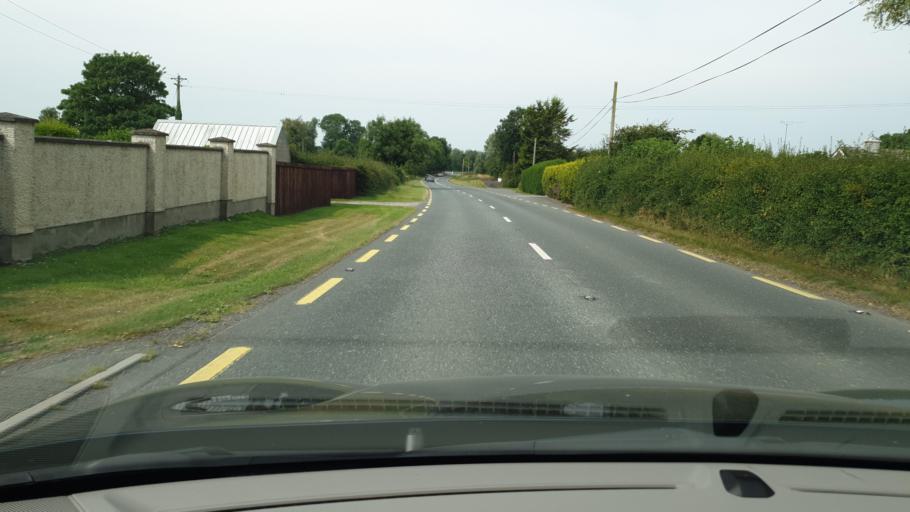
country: IE
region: Leinster
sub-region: An Mhi
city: Newtown Trim
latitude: 53.6296
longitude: -6.7811
